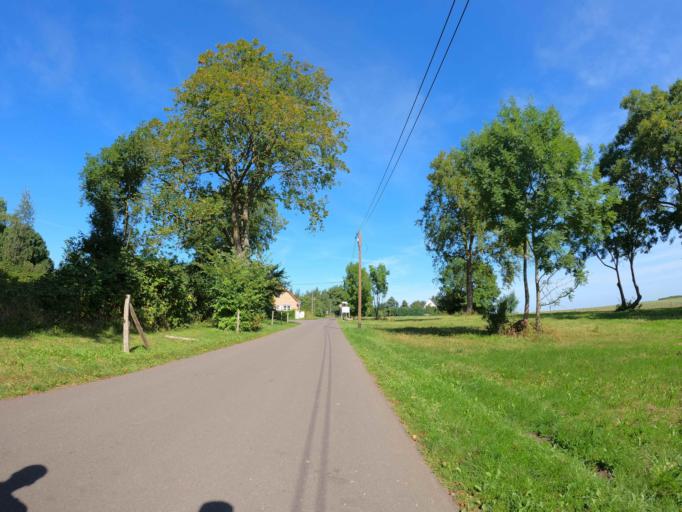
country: DE
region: Mecklenburg-Vorpommern
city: Kramerhof
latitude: 54.3739
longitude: 13.0483
